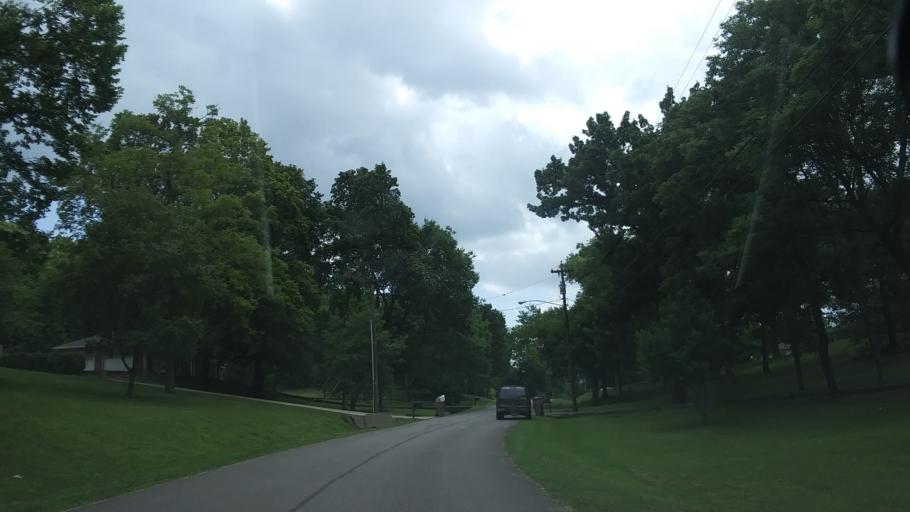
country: US
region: Tennessee
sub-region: Davidson County
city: Belle Meade
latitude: 36.1368
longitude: -86.8697
